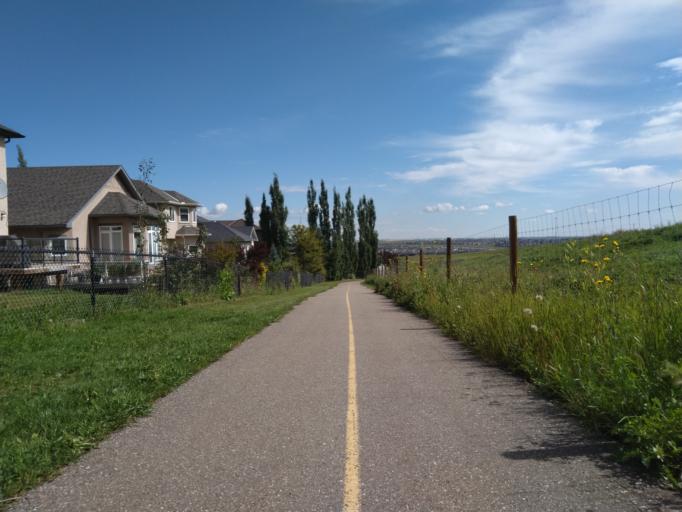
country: CA
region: Alberta
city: Calgary
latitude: 51.1552
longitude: -114.1479
